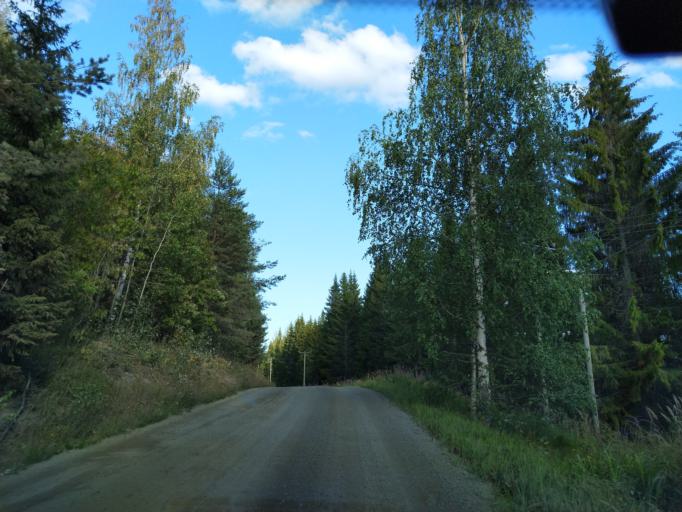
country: FI
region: Central Finland
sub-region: Jaemsae
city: Kuhmoinen
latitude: 61.6944
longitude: 24.9365
